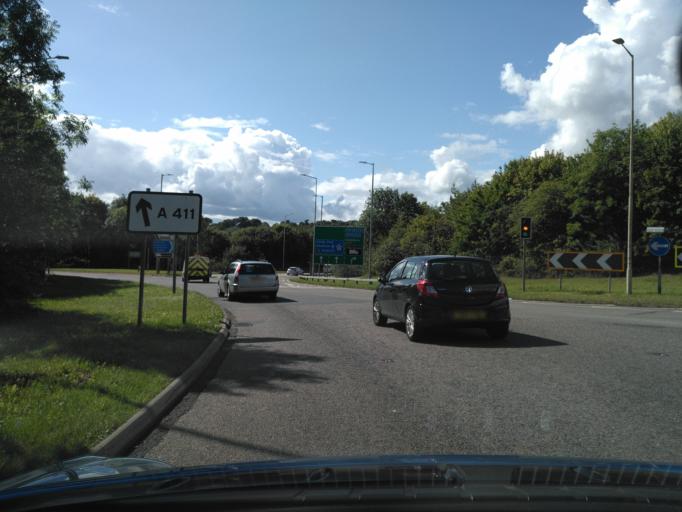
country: GB
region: England
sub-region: Hertfordshire
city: Abbots Langley
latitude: 51.6840
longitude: -0.4293
